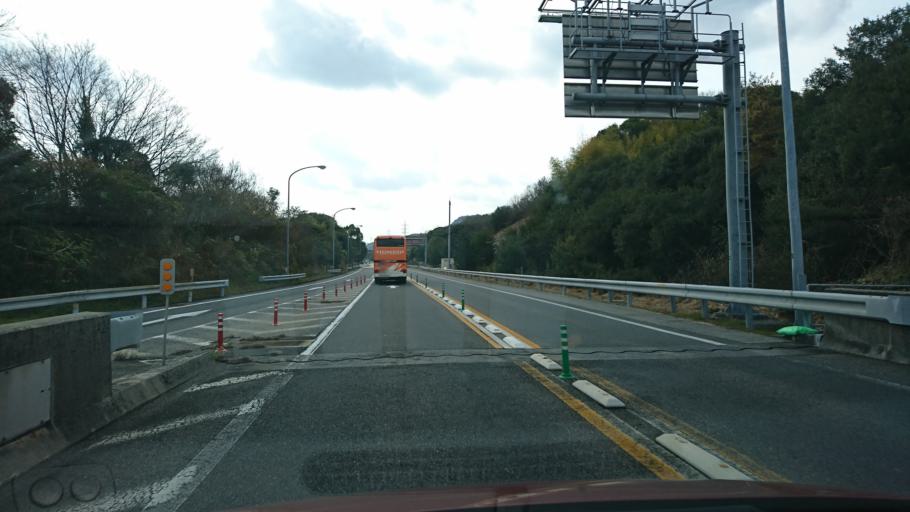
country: JP
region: Hiroshima
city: Innoshima
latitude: 34.2475
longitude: 133.0483
